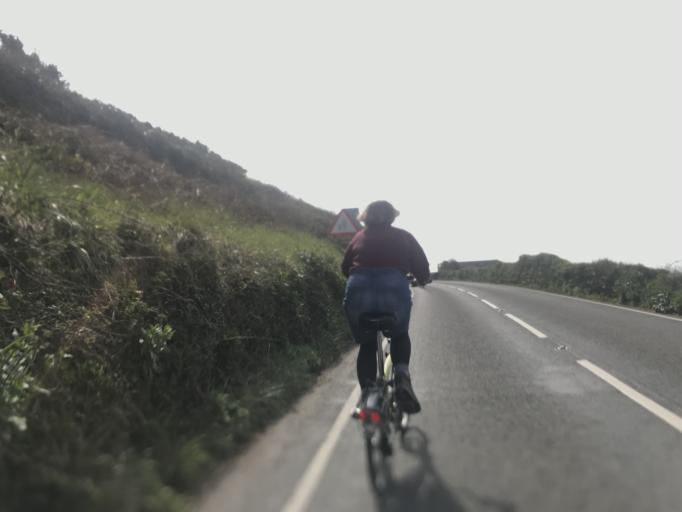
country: GB
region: England
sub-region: Devon
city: Braunton
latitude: 51.1244
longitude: -4.2405
